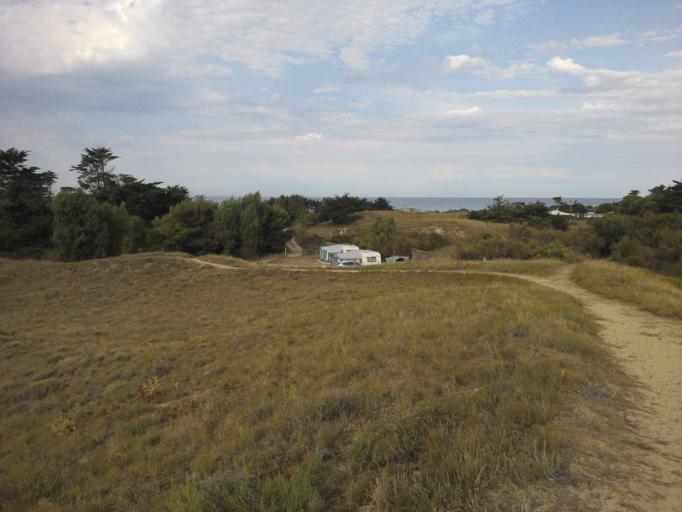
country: FR
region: Poitou-Charentes
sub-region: Departement de la Charente-Maritime
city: Saint-Denis-d'Oleron
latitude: 46.0153
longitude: -1.3934
